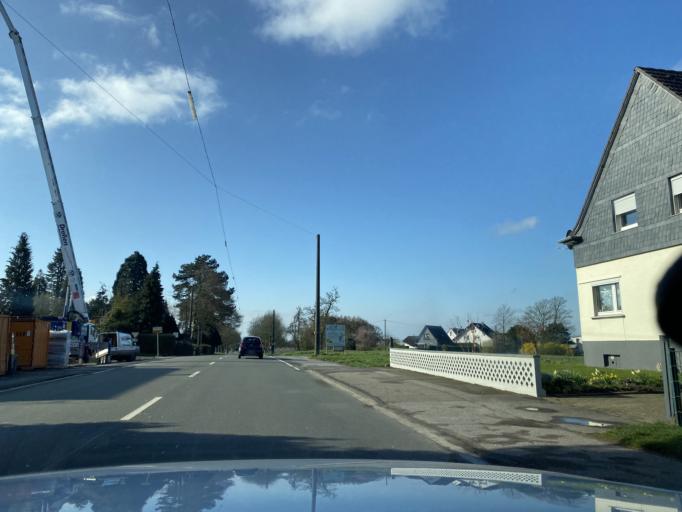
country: DE
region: North Rhine-Westphalia
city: Burscheid
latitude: 51.0799
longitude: 7.1305
